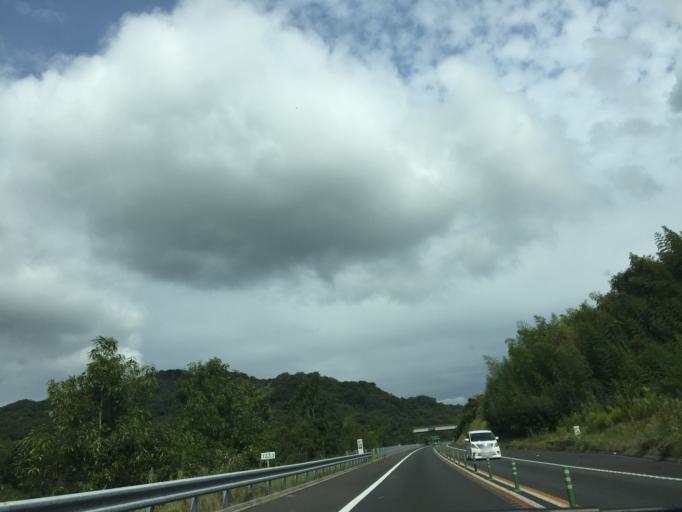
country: JP
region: Kagawa
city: Shido
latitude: 34.2550
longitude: 134.2909
